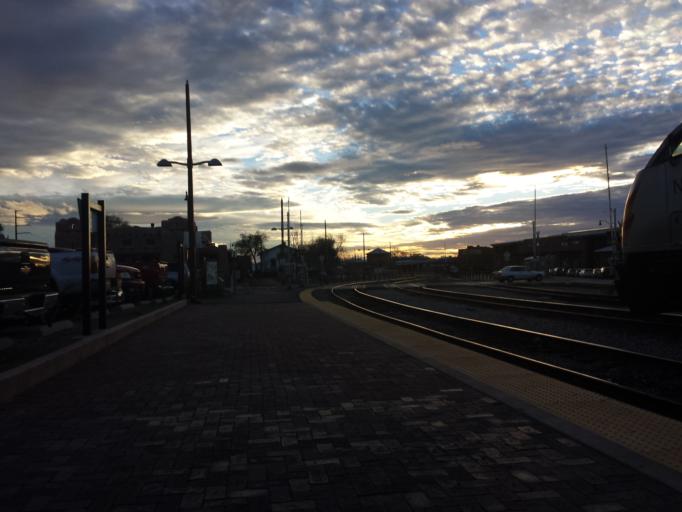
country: US
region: New Mexico
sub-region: Santa Fe County
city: Santa Fe
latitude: 35.6842
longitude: -105.9469
